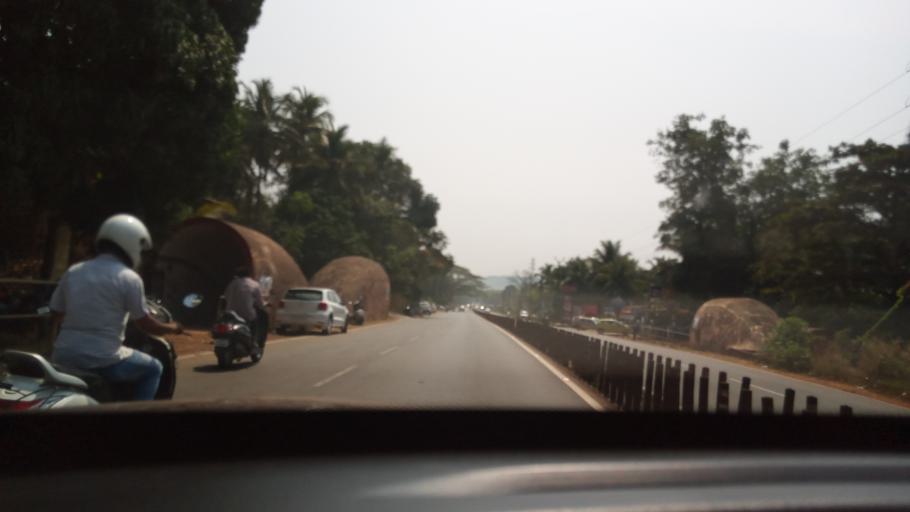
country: IN
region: Goa
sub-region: South Goa
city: Raia
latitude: 15.3279
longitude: 73.9340
